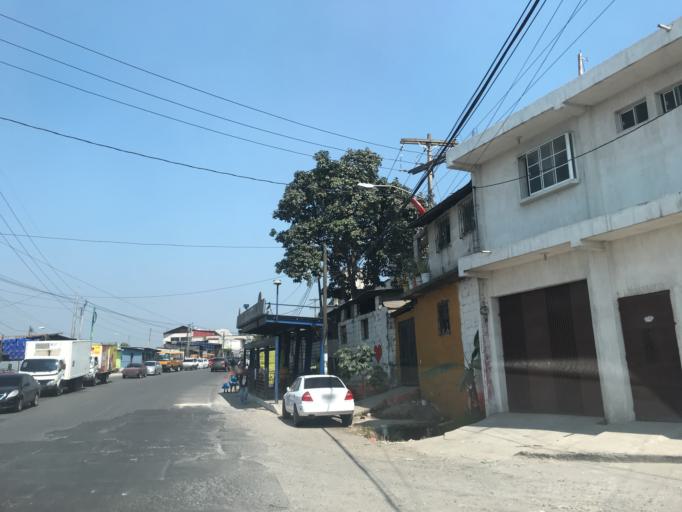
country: GT
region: Guatemala
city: Villa Nueva
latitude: 14.5428
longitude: -90.5577
